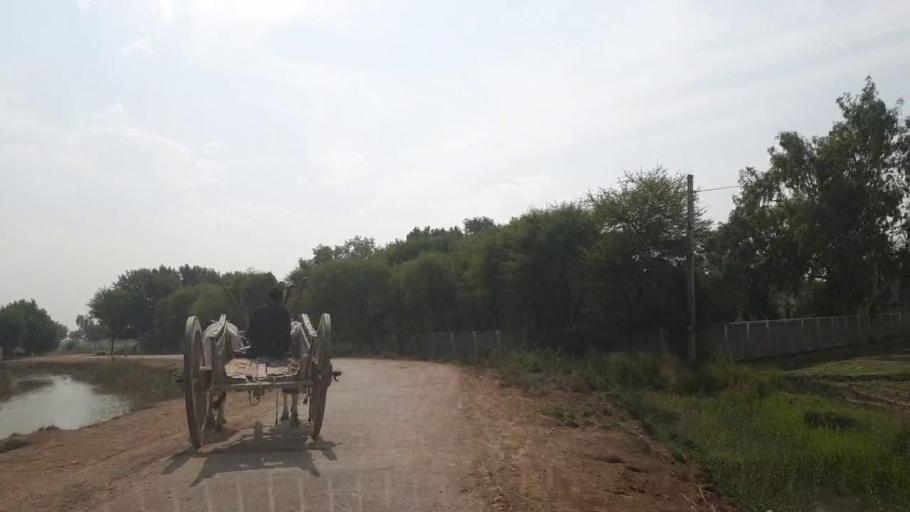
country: PK
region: Sindh
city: Rajo Khanani
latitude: 24.9598
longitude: 69.0089
